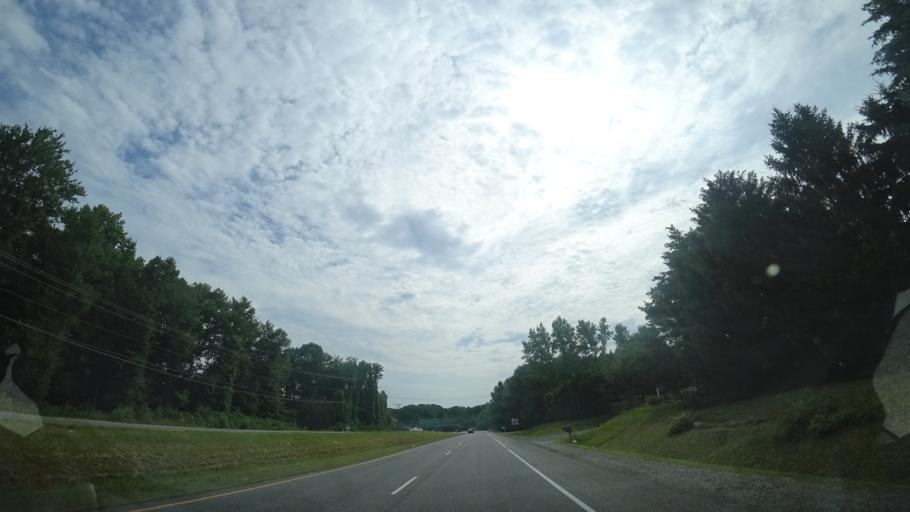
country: US
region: Virginia
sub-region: Spotsylvania County
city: Spotsylvania
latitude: 38.2396
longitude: -77.5404
